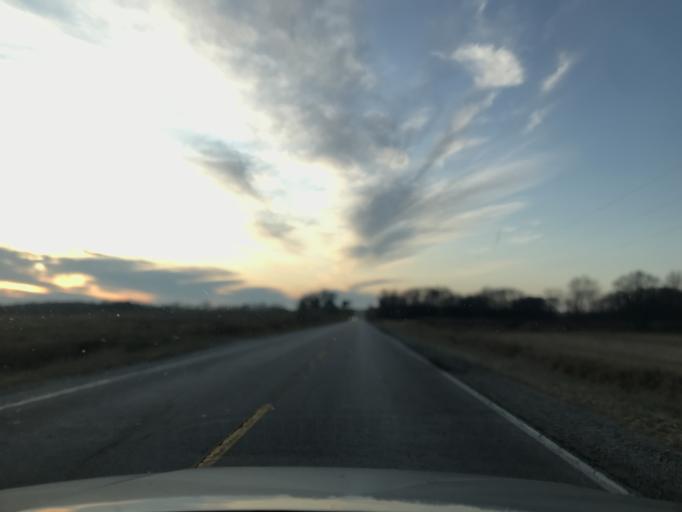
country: US
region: Illinois
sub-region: Henderson County
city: Oquawka
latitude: 41.0190
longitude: -90.8229
